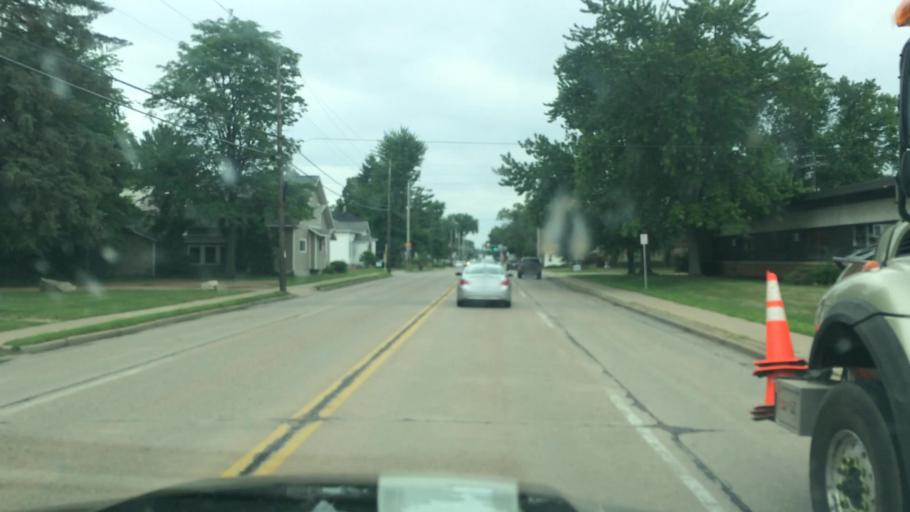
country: US
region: Wisconsin
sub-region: Portage County
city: Stevens Point
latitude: 44.5260
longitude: -89.5748
